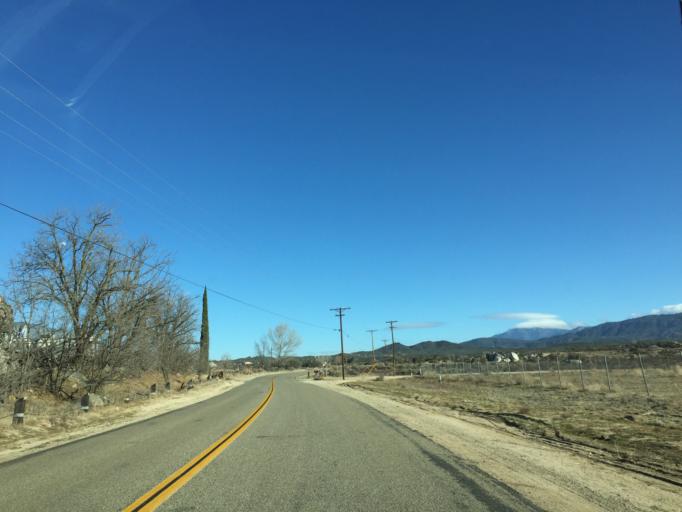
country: US
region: California
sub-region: Riverside County
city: Anza
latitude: 33.5505
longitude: -116.7354
